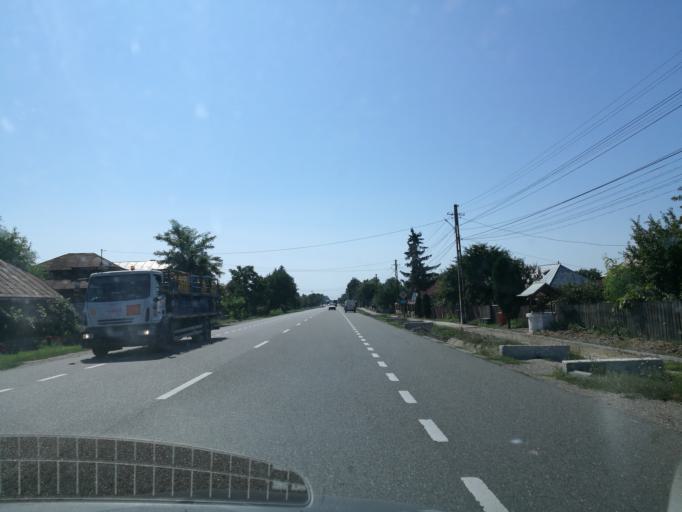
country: RO
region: Bacau
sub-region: Comuna Filipesti
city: Filipesti
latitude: 46.7443
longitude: 26.8849
